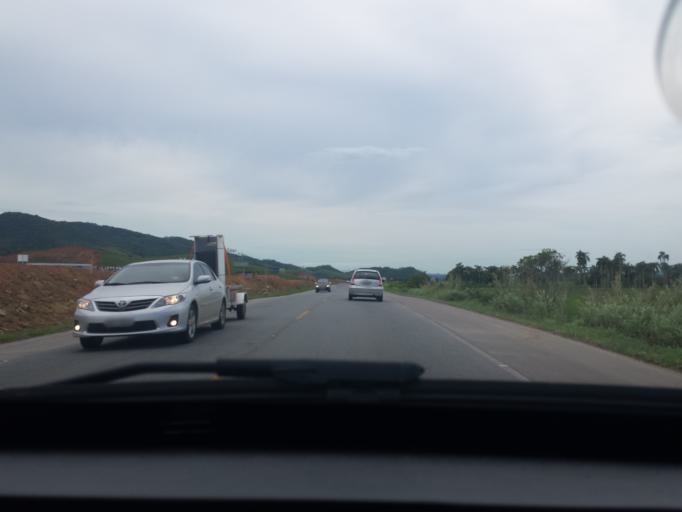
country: BR
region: Santa Catarina
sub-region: Gaspar
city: Gaspar
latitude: -26.8897
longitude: -48.8810
